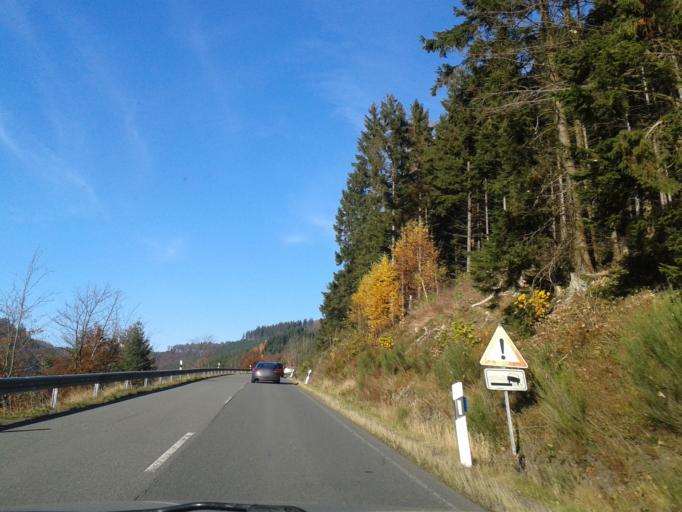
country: DE
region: North Rhine-Westphalia
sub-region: Regierungsbezirk Arnsberg
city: Bad Berleburg
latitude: 51.1133
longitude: 8.4312
